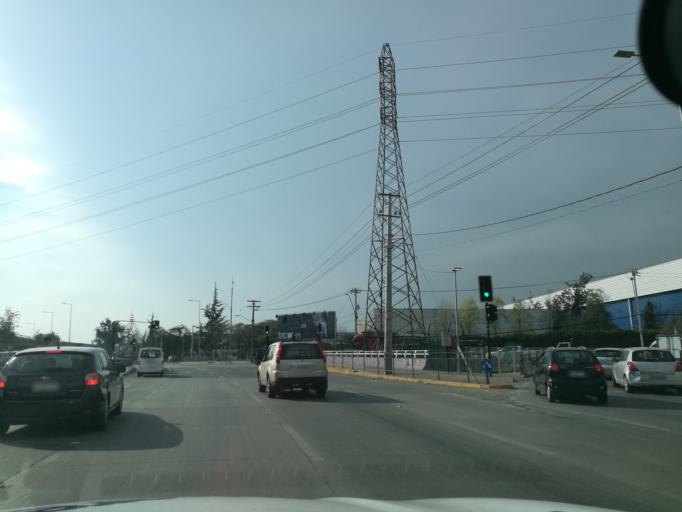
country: CL
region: Santiago Metropolitan
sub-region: Provincia de Santiago
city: Santiago
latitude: -33.4864
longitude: -70.6186
